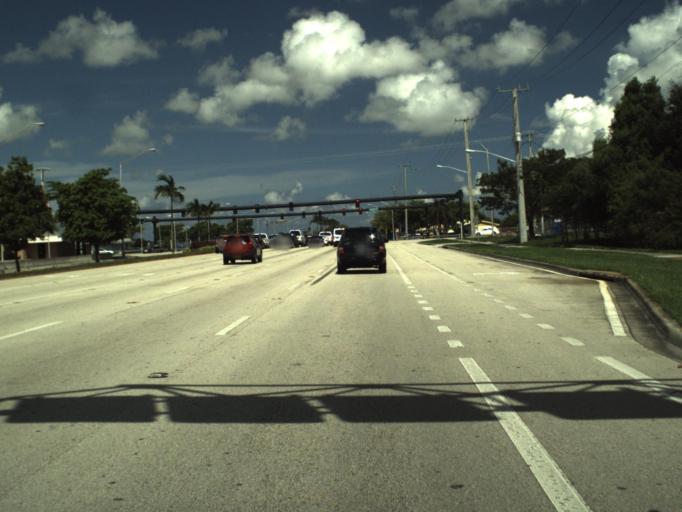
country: US
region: Florida
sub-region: Broward County
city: Miramar
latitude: 25.9945
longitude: -80.2494
